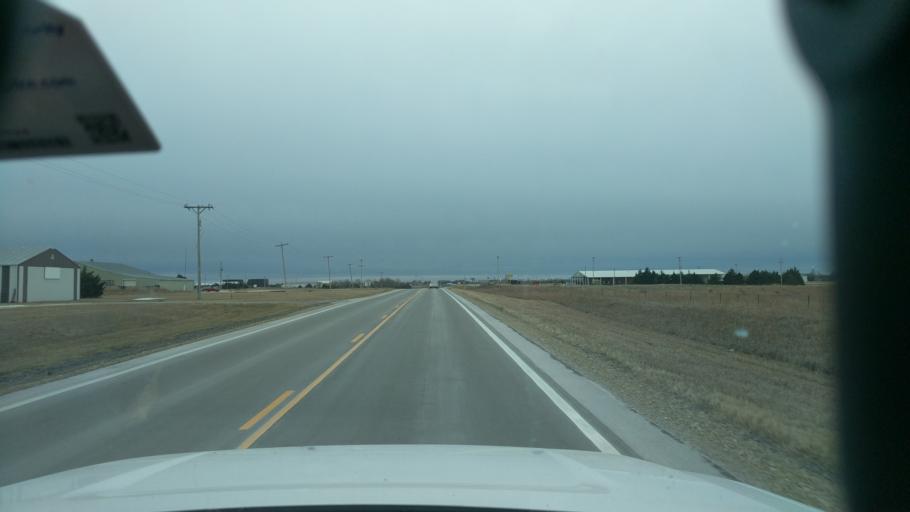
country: US
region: Kansas
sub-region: Dickinson County
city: Herington
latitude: 38.6848
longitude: -96.9304
